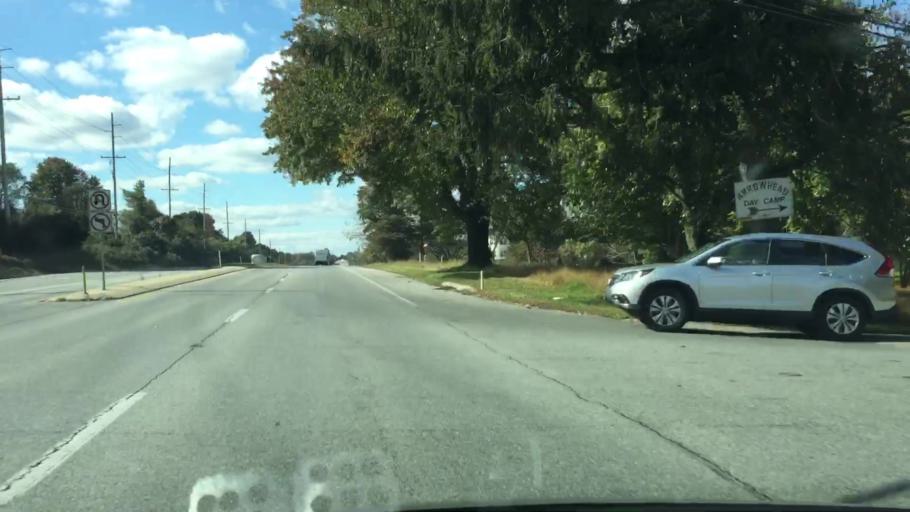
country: US
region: Pennsylvania
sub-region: Chester County
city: Malvern
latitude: 39.9651
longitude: -75.5008
